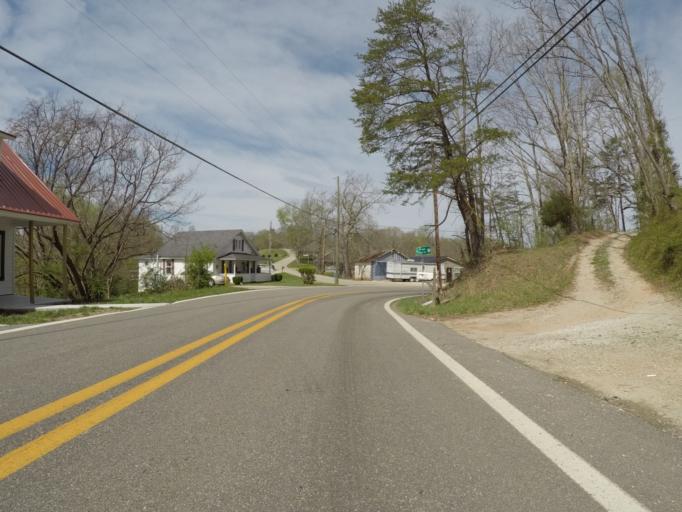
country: US
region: West Virginia
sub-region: Cabell County
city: Pea Ridge
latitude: 38.3448
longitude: -82.3608
